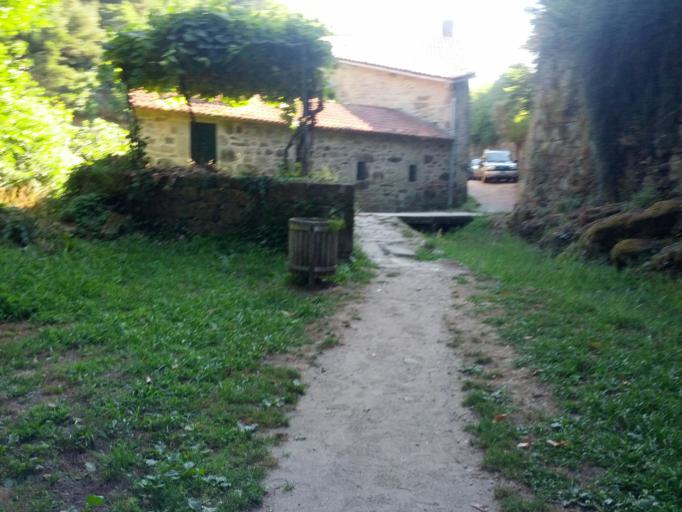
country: ES
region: Galicia
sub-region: Provincia da Coruna
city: Santiago de Compostela
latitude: 42.8797
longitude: -8.5599
